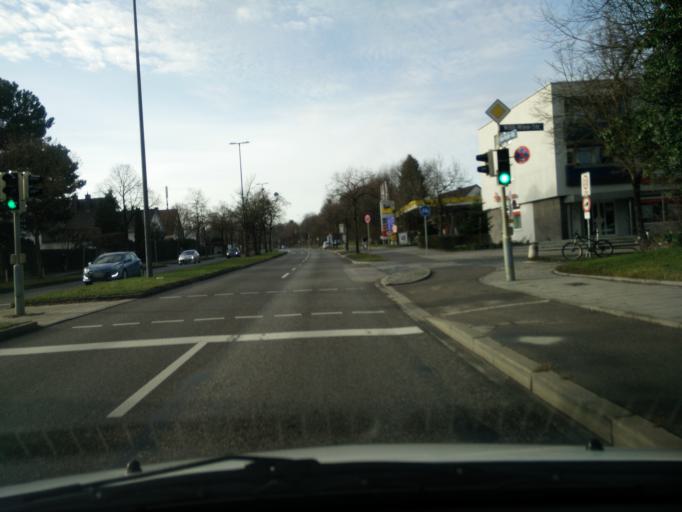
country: DE
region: Bavaria
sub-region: Upper Bavaria
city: Pasing
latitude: 48.1775
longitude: 11.4685
